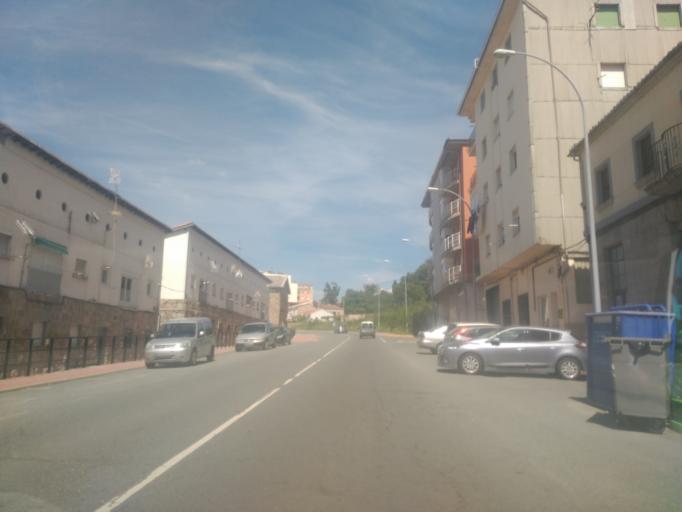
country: ES
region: Castille and Leon
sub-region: Provincia de Salamanca
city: Bejar
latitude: 40.3858
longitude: -5.7542
